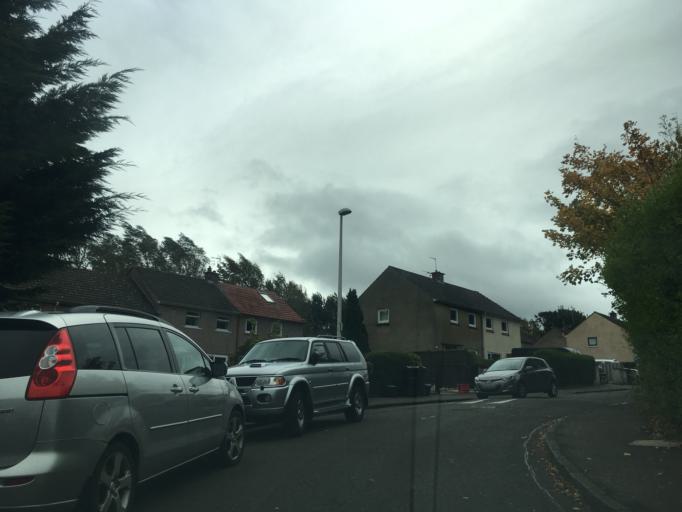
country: GB
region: Scotland
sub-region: Edinburgh
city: Colinton
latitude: 55.9076
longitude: -3.2227
